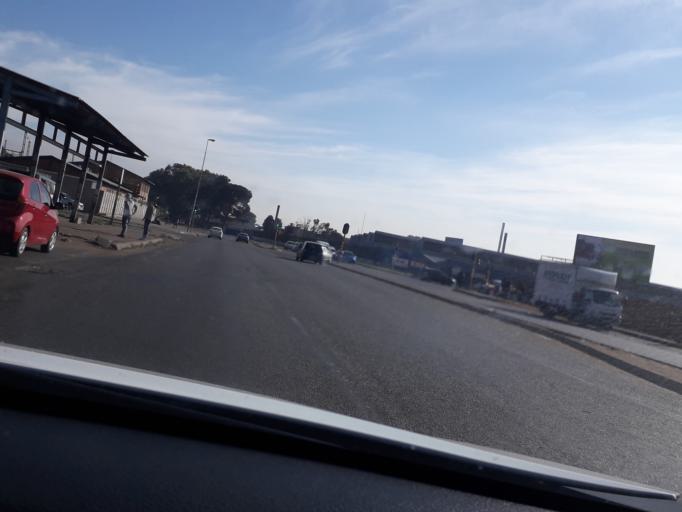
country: ZA
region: Gauteng
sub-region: Ekurhuleni Metropolitan Municipality
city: Boksburg
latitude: -26.1671
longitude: 28.2060
